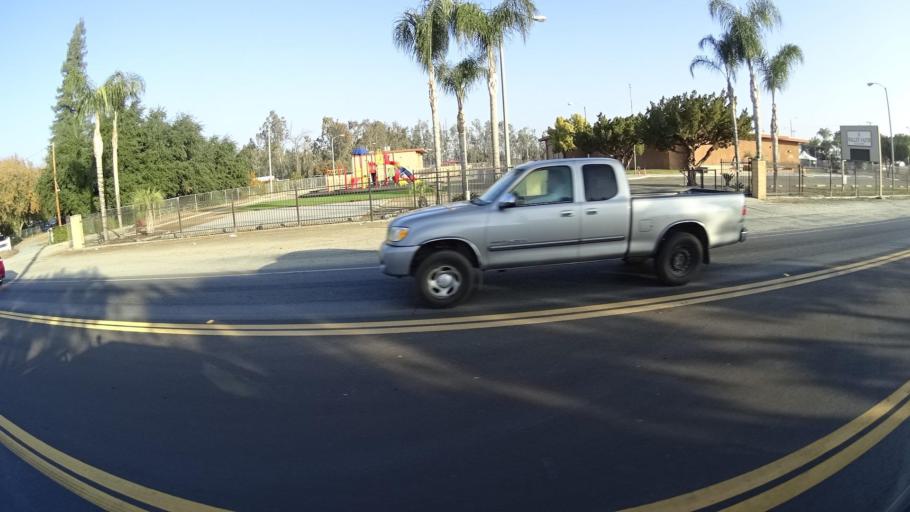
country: US
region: California
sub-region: Kern County
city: Delano
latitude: 35.7904
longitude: -119.2248
